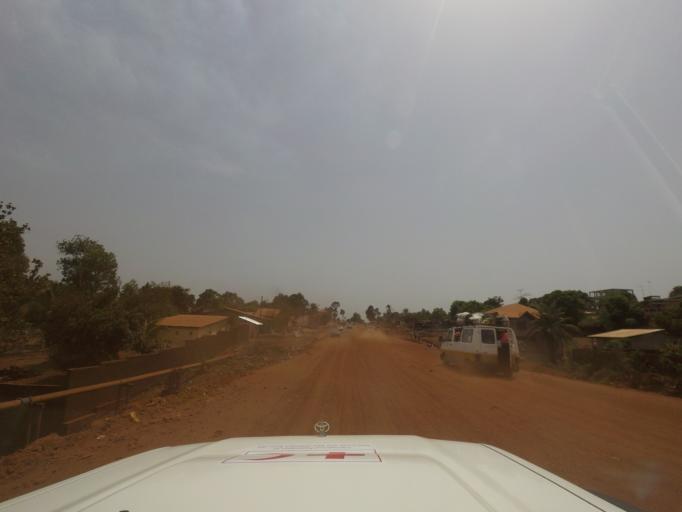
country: GN
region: Kindia
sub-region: Prefecture de Dubreka
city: Dubreka
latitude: 9.7090
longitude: -13.4892
